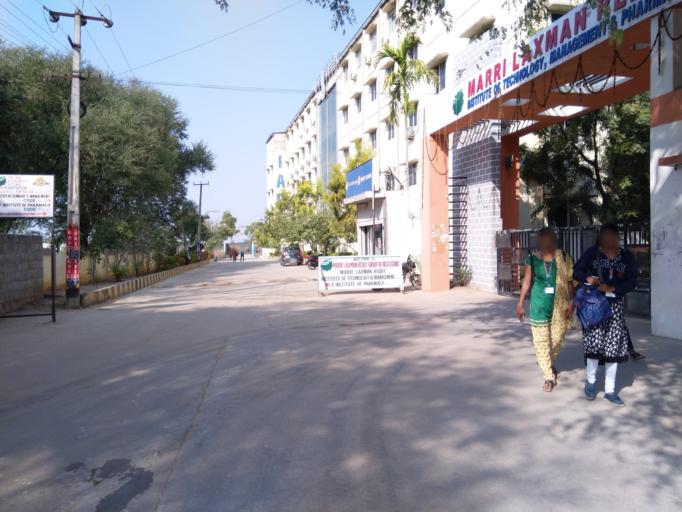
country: IN
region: Telangana
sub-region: Rangareddi
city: Quthbullapur
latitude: 17.5994
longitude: 78.4167
